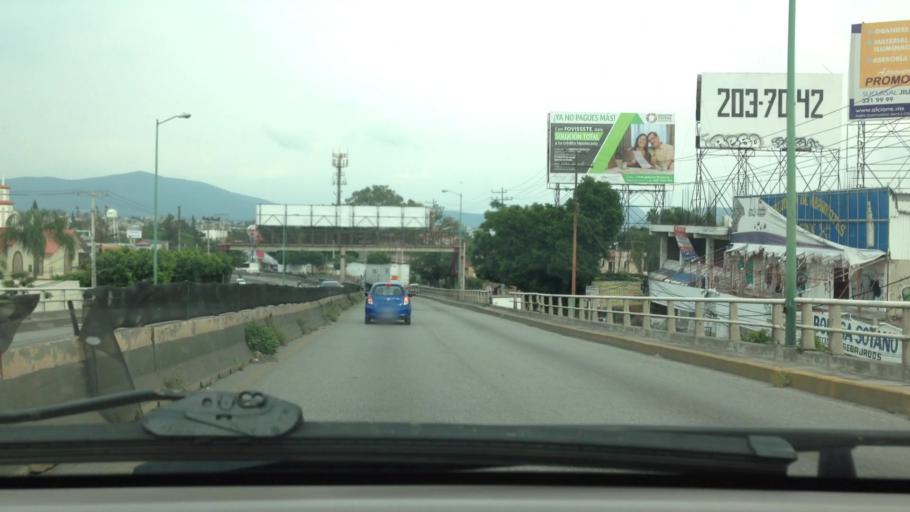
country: MX
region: Morelos
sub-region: Tepoztlan
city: Loma Bonita
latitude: 18.9199
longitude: -99.1972
